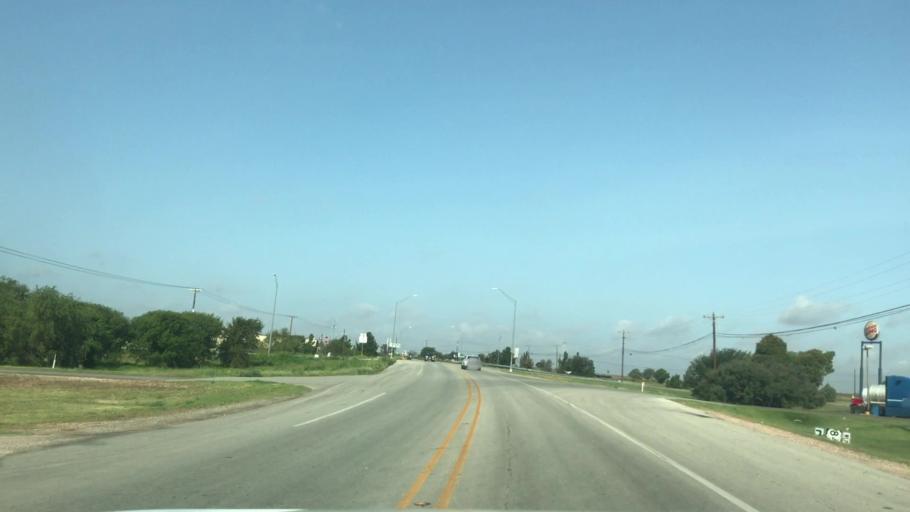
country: US
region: Texas
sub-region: Scurry County
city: Snyder
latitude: 32.7047
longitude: -100.8657
